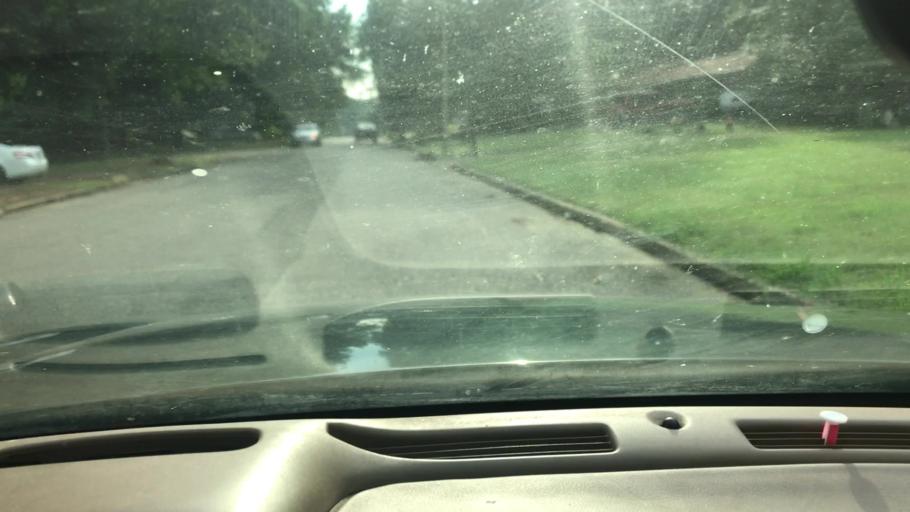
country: US
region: Mississippi
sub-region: De Soto County
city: Southaven
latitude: 35.0466
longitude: -90.0153
